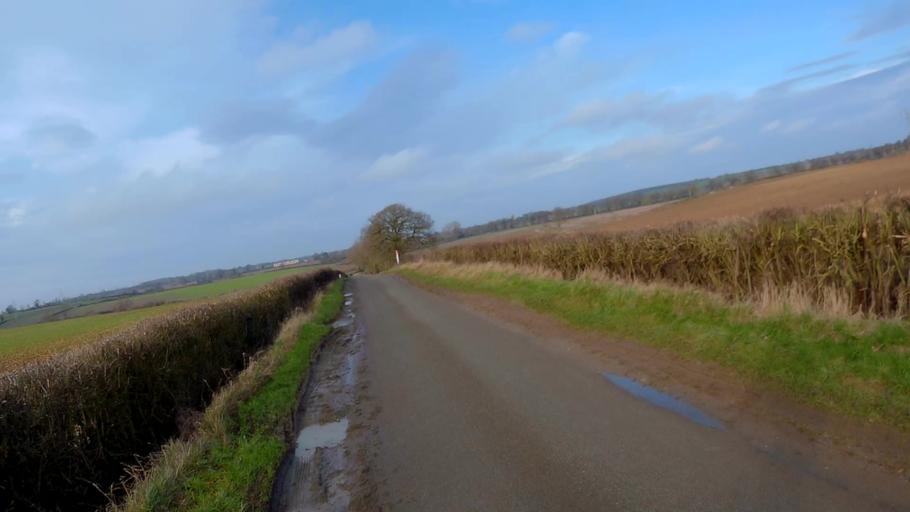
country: GB
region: England
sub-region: Lincolnshire
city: Bourne
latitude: 52.7688
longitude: -0.4226
